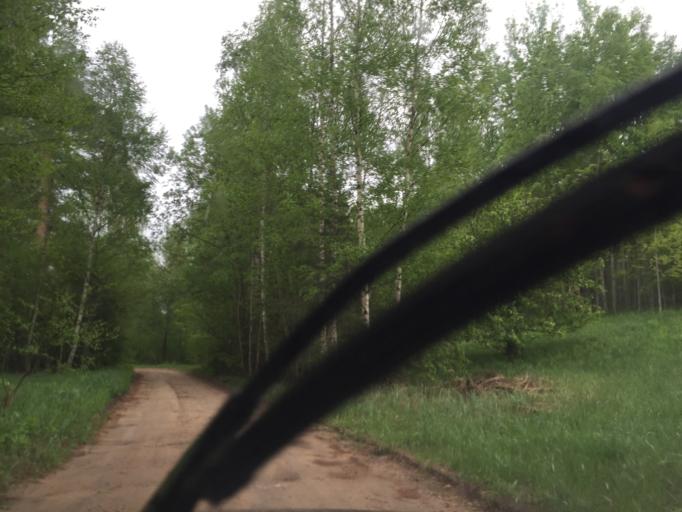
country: LV
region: Kegums
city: Kegums
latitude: 56.7338
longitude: 24.7535
